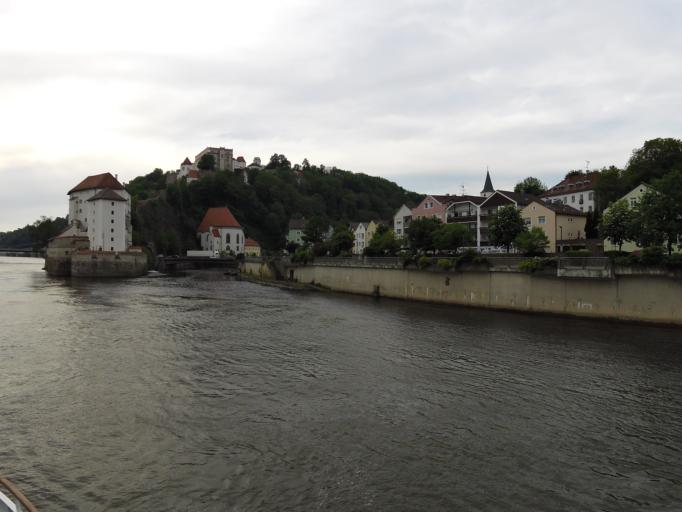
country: DE
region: Bavaria
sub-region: Lower Bavaria
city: Salzweg
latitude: 48.5751
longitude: 13.4771
